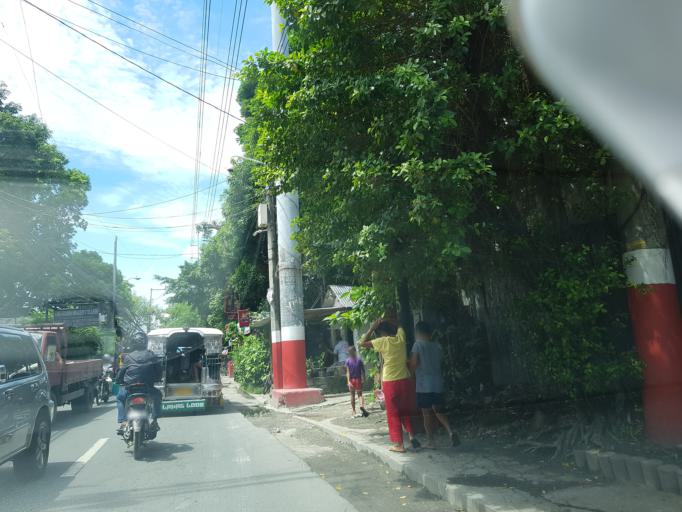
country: PH
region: Calabarzon
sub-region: Province of Rizal
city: Taguig
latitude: 14.5174
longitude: 121.0728
